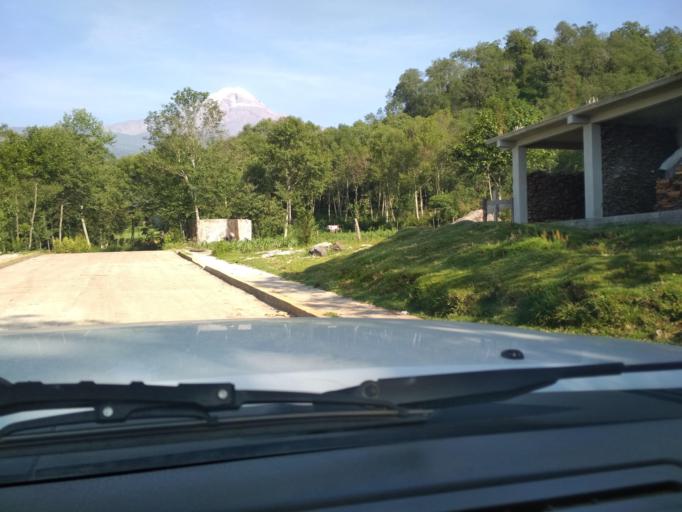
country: MX
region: Veracruz
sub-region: La Perla
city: Chilapa
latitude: 18.9853
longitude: -97.1653
